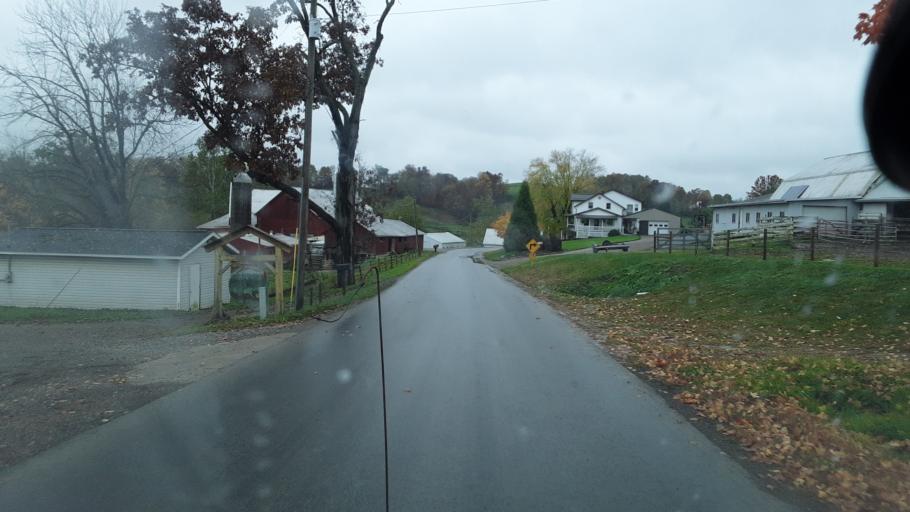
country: US
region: Ohio
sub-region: Holmes County
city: Millersburg
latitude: 40.4536
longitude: -81.8103
